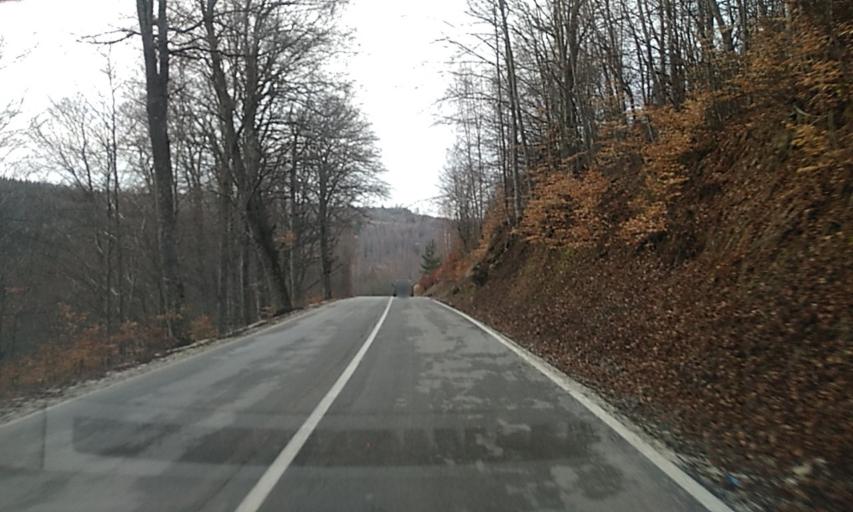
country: RS
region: Central Serbia
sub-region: Pcinjski Okrug
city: Bosilegrad
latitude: 42.6512
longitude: 22.3827
